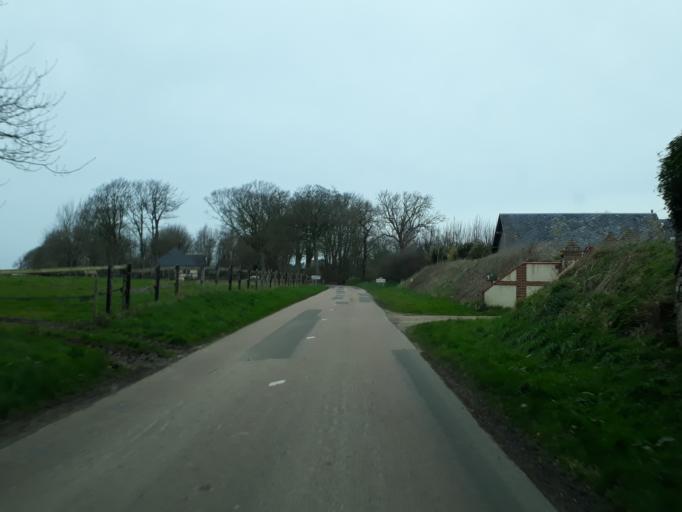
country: FR
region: Haute-Normandie
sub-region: Departement de la Seine-Maritime
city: Les Loges
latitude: 49.7194
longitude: 0.2830
